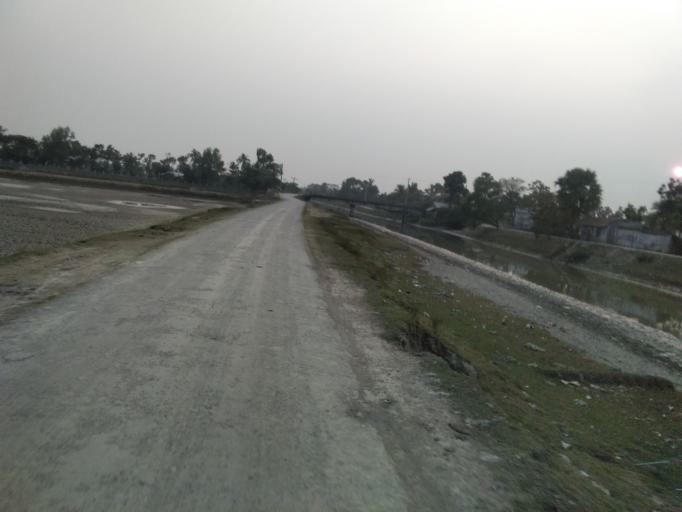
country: BD
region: Khulna
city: Satkhira
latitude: 22.6493
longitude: 89.0135
